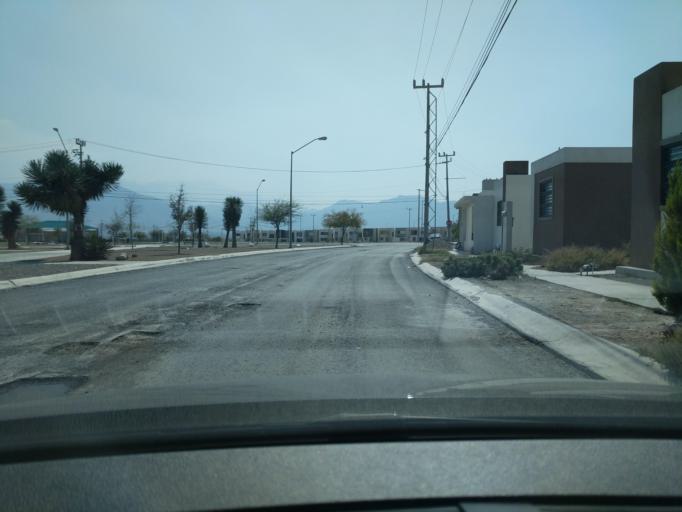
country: MX
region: Nuevo Leon
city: Garcia
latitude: 25.8168
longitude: -100.5399
